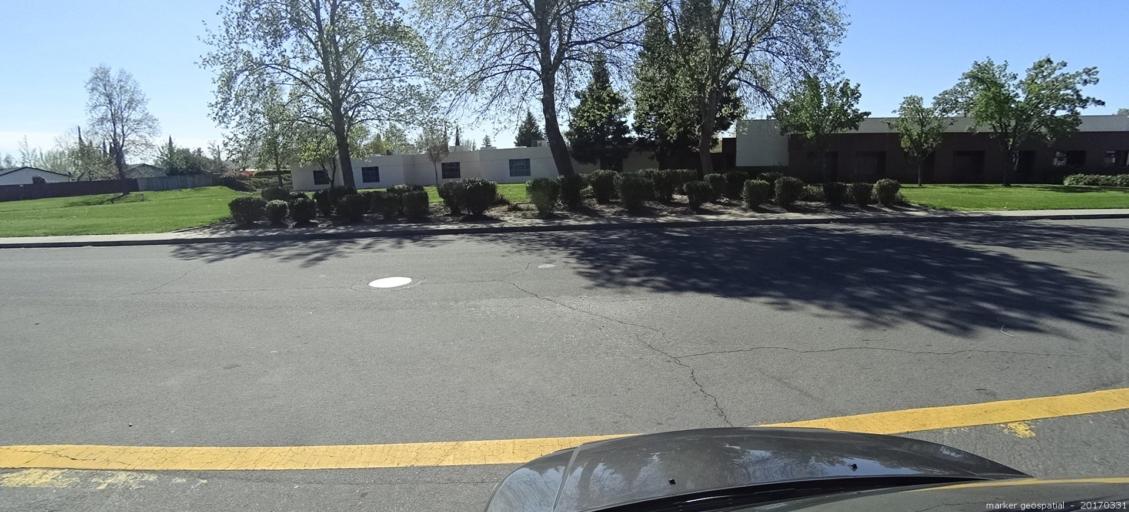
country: US
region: California
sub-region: Sacramento County
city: Parkway
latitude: 38.4712
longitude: -121.4412
